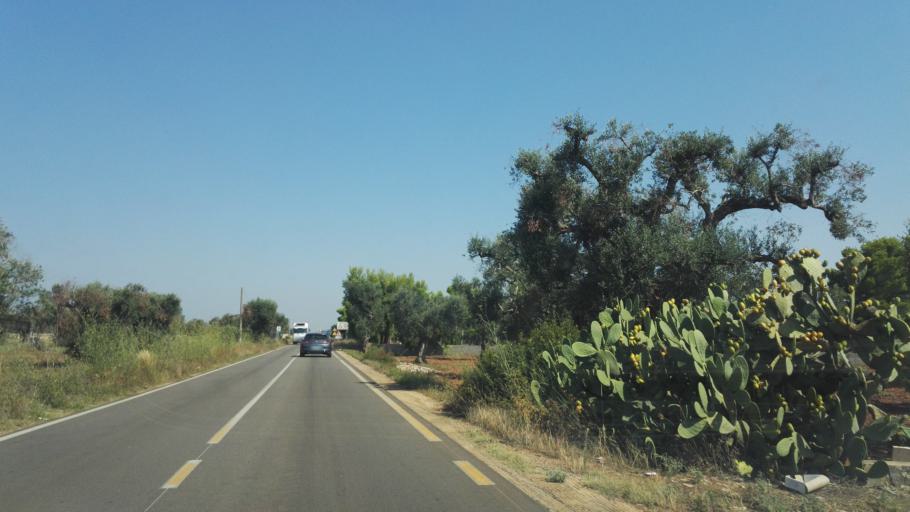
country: IT
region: Apulia
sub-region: Provincia di Lecce
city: Nardo
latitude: 40.1801
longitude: 17.9755
